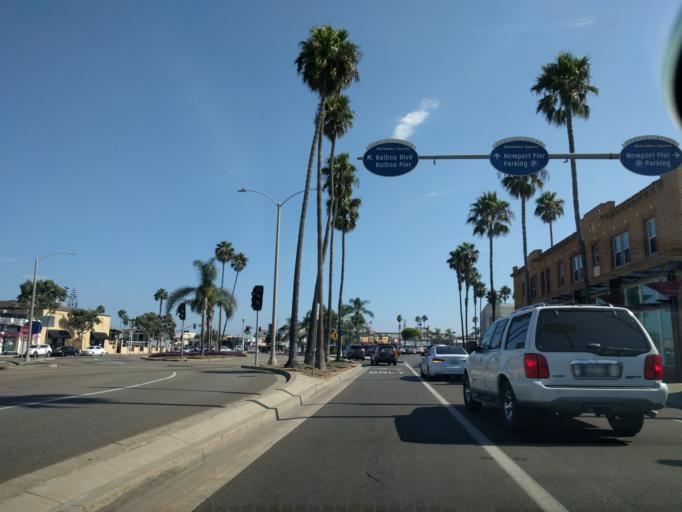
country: US
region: California
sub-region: Orange County
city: Newport Beach
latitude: 33.6100
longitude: -117.9288
